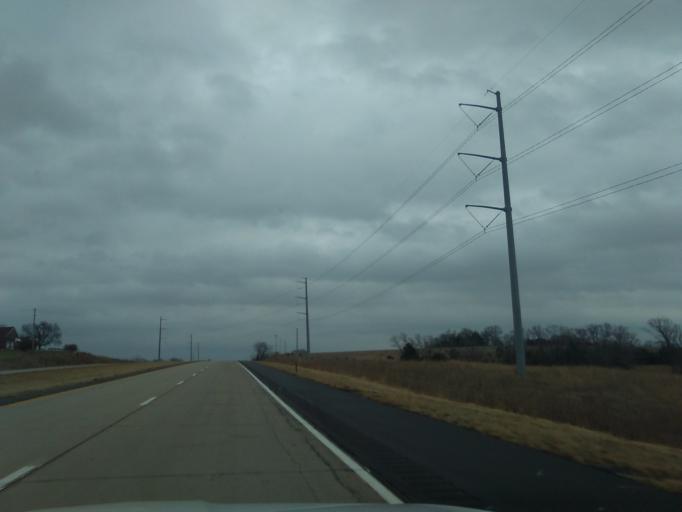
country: US
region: Nebraska
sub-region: Otoe County
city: Syracuse
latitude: 40.6683
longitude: -96.1292
